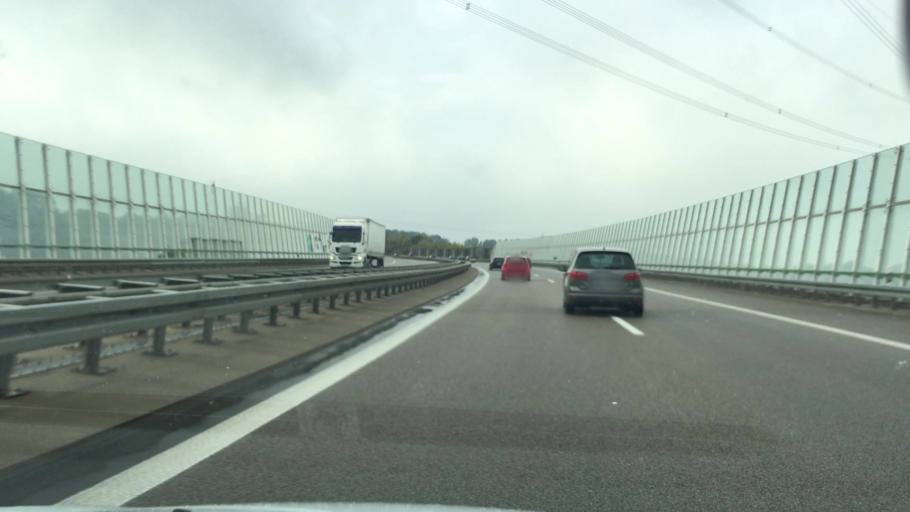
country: DE
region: Saxony
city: Hartmannsdorf
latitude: 50.8635
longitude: 12.8159
